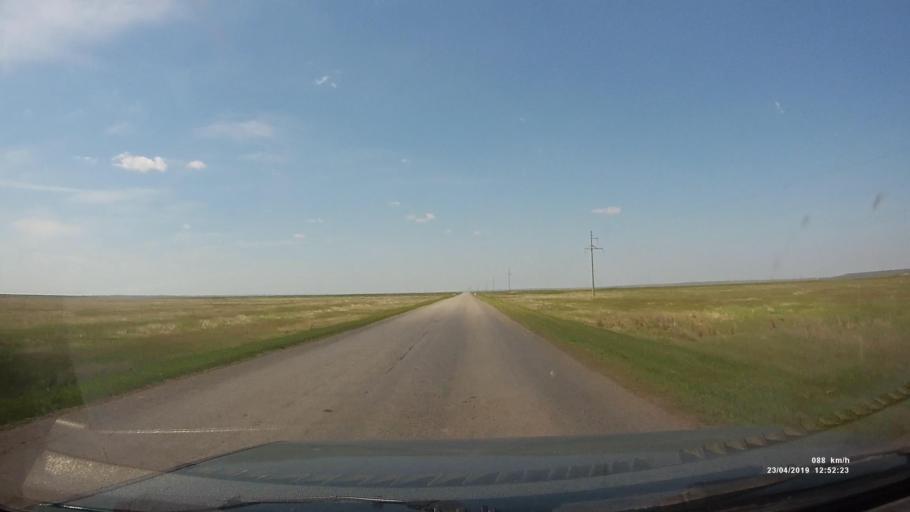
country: RU
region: Kalmykiya
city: Yashalta
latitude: 46.5641
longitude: 42.6103
